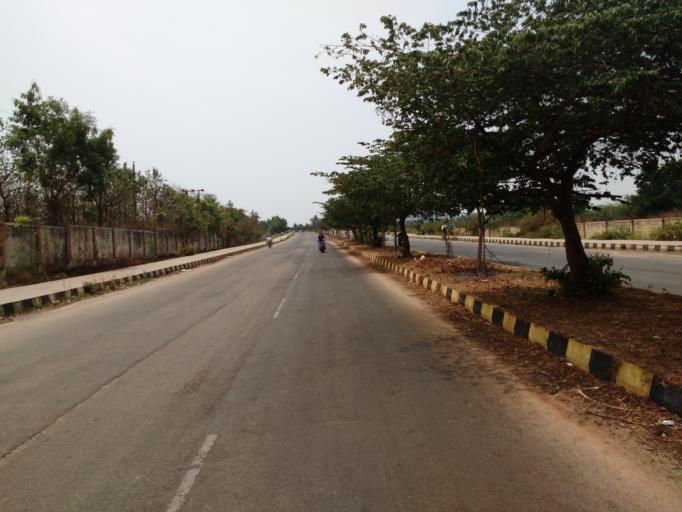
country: IN
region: Karnataka
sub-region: Hassan
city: Hassan
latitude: 13.0147
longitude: 76.1187
